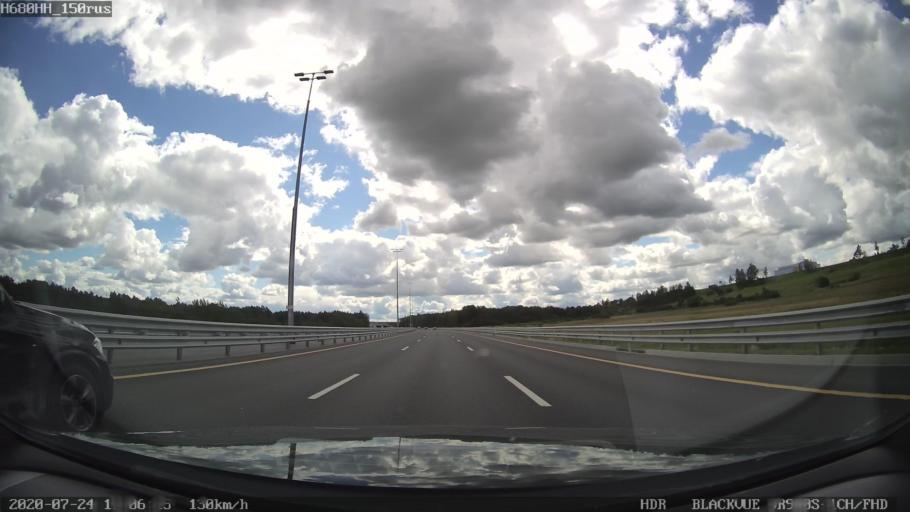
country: RU
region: St.-Petersburg
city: Shushary
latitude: 59.7656
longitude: 30.3704
